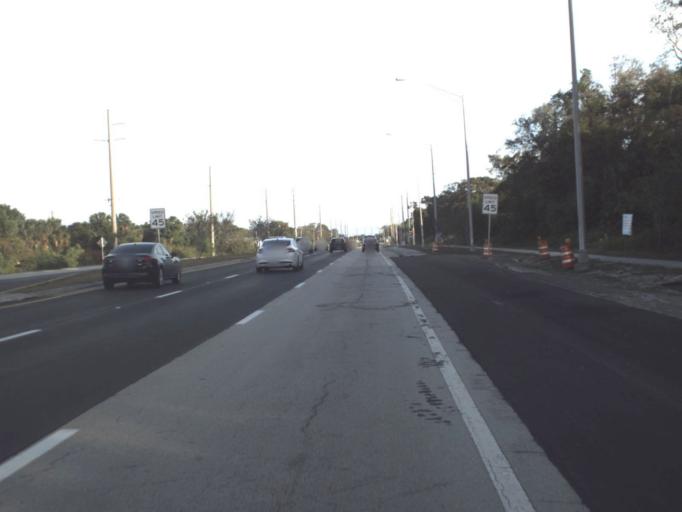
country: US
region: Florida
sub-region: Brevard County
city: South Patrick Shores
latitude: 28.1709
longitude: -80.6468
